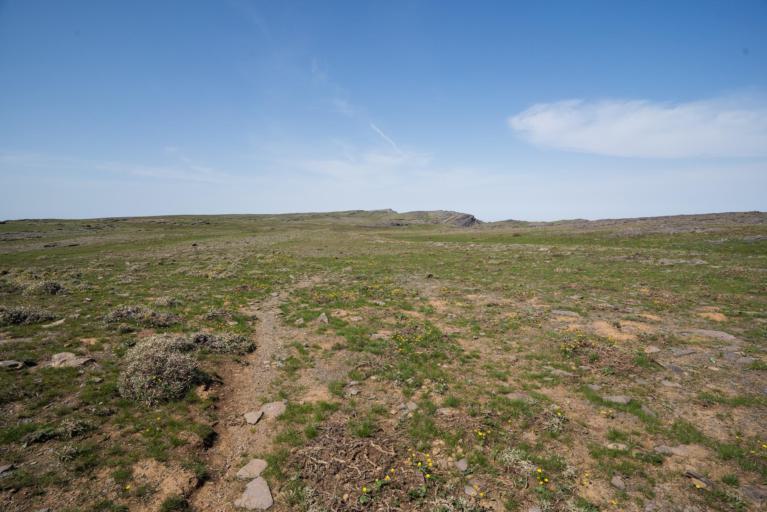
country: KZ
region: Ongtustik Qazaqstan
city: Kentau
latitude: 43.8480
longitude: 68.4752
